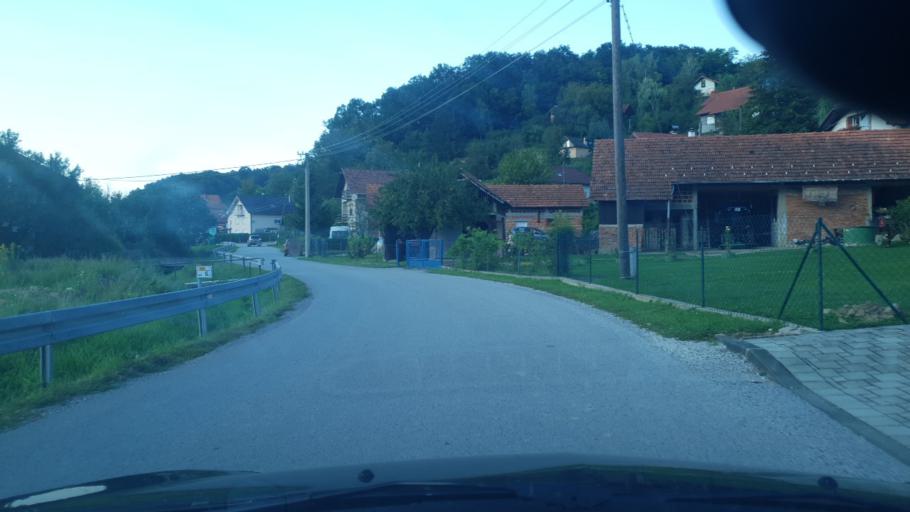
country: HR
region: Krapinsko-Zagorska
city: Zabok
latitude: 46.0287
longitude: 15.8976
